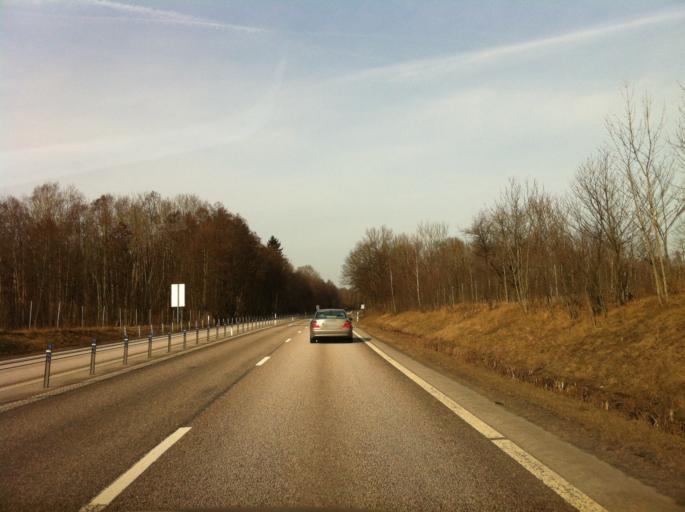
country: SE
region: Vaestra Goetaland
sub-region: Skovde Kommun
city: Stopen
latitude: 58.4605
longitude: 13.8471
